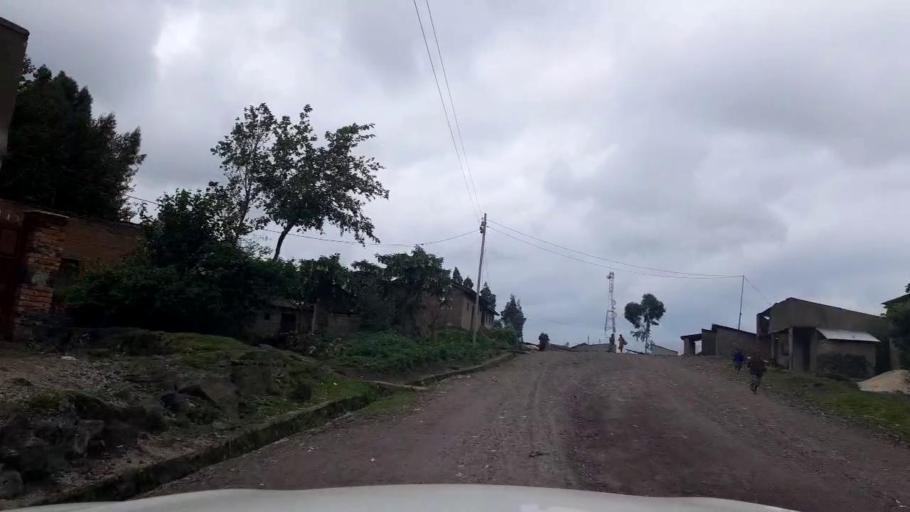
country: RW
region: Northern Province
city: Musanze
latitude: -1.5912
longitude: 29.4671
